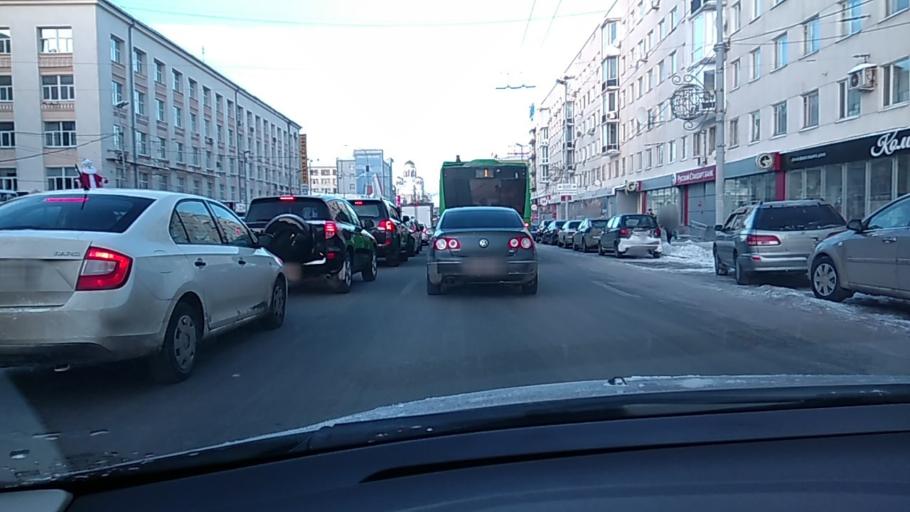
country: RU
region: Sverdlovsk
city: Yekaterinburg
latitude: 56.8376
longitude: 60.6121
